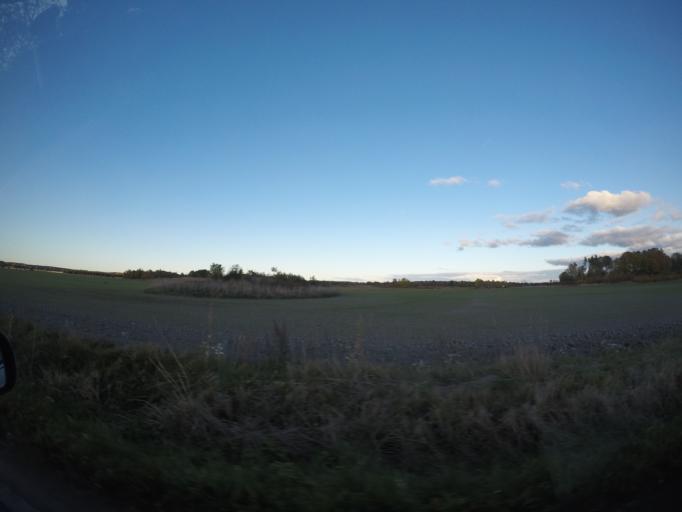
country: SE
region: Vaestmanland
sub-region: Vasteras
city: Vasteras
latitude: 59.5378
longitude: 16.4743
